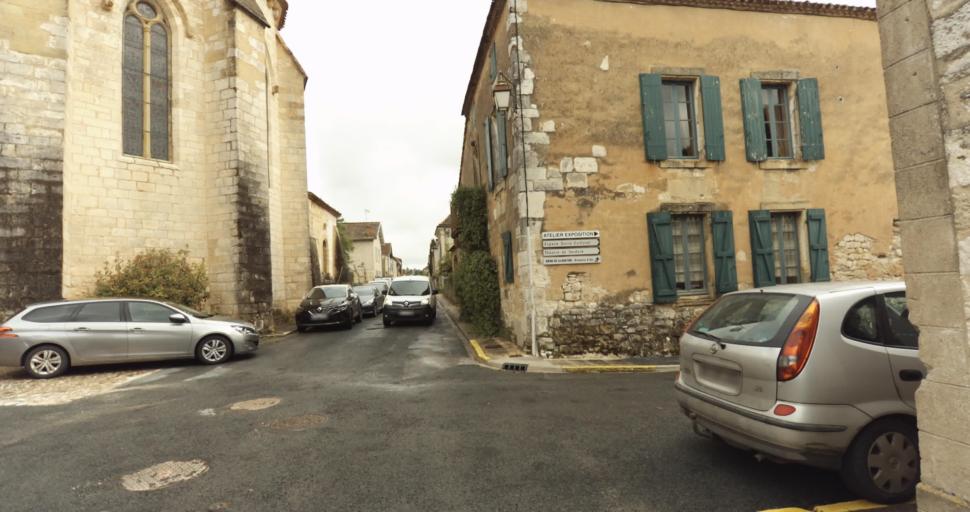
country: FR
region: Aquitaine
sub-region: Departement de la Dordogne
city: Belves
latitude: 44.6804
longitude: 0.8953
